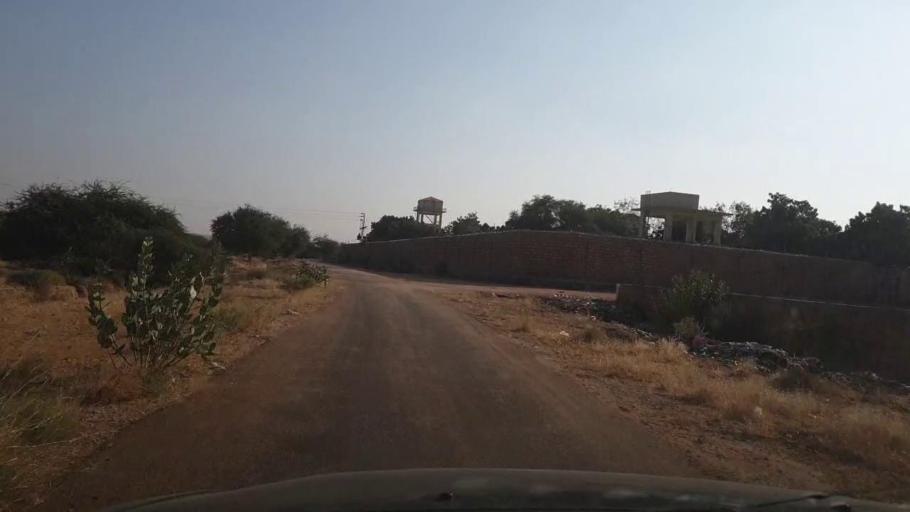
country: PK
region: Sindh
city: Jamshoro
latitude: 25.3296
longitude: 67.8451
